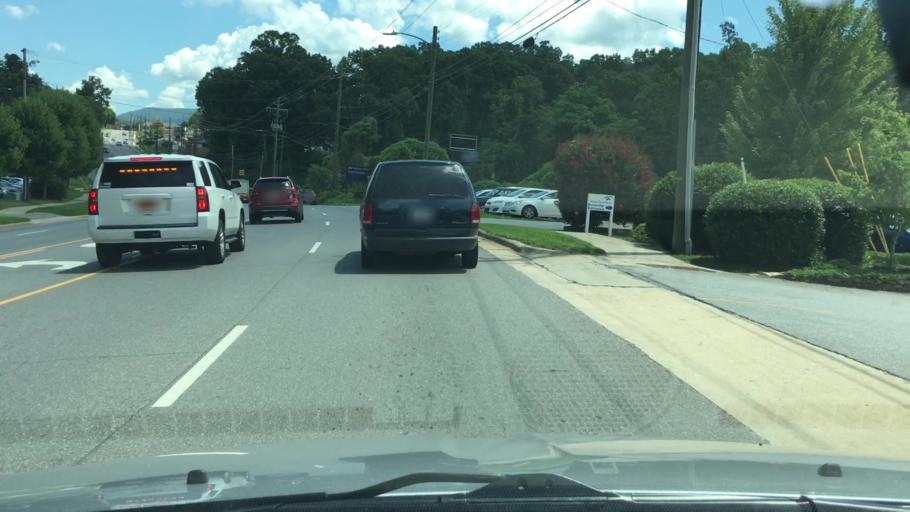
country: US
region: North Carolina
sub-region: Buncombe County
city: Asheville
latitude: 35.5875
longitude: -82.4932
